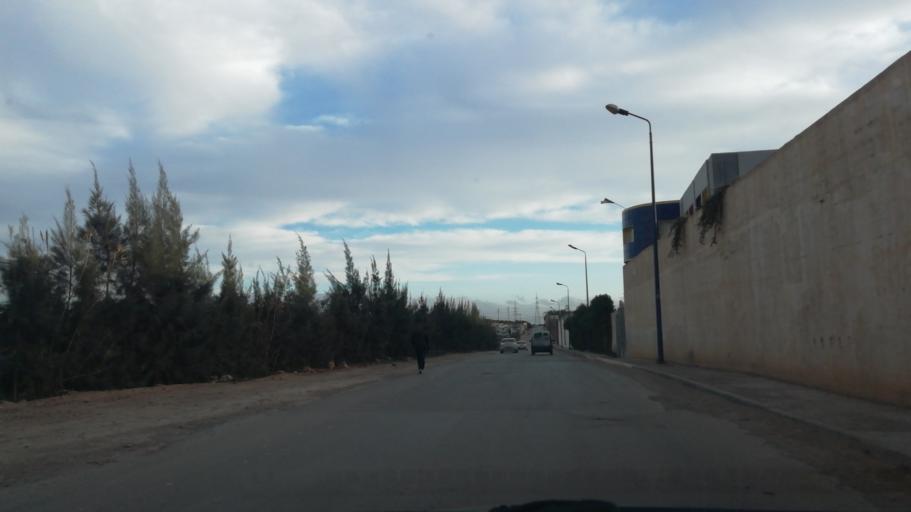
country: DZ
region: Oran
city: Es Senia
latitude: 35.6850
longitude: -0.5871
